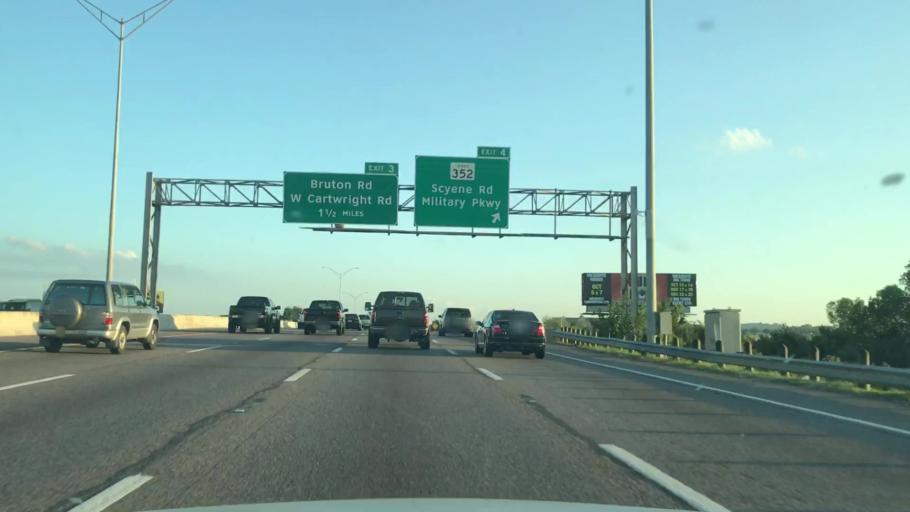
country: US
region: Texas
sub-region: Dallas County
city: Mesquite
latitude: 32.7729
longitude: -96.6238
